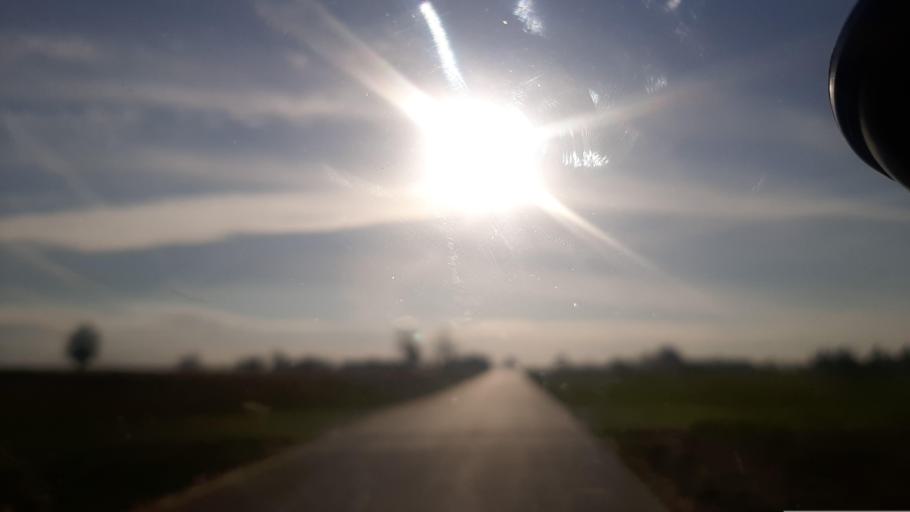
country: PL
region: Lublin Voivodeship
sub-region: Powiat lubelski
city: Garbow
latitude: 51.3903
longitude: 22.3456
